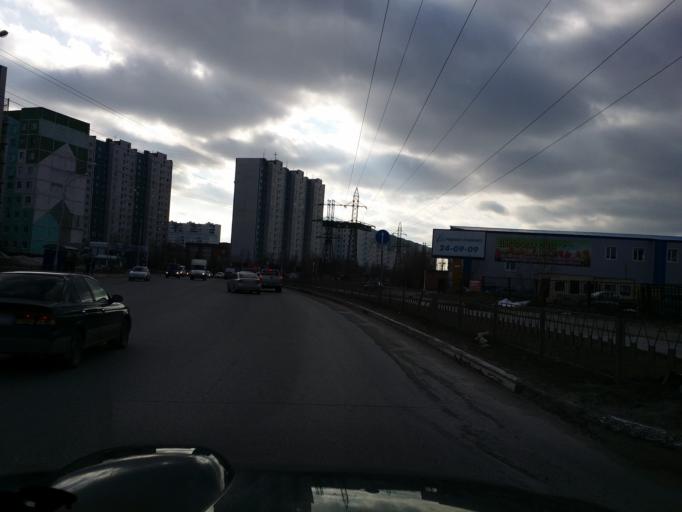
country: RU
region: Khanty-Mansiyskiy Avtonomnyy Okrug
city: Nizhnevartovsk
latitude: 60.9543
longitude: 76.5951
